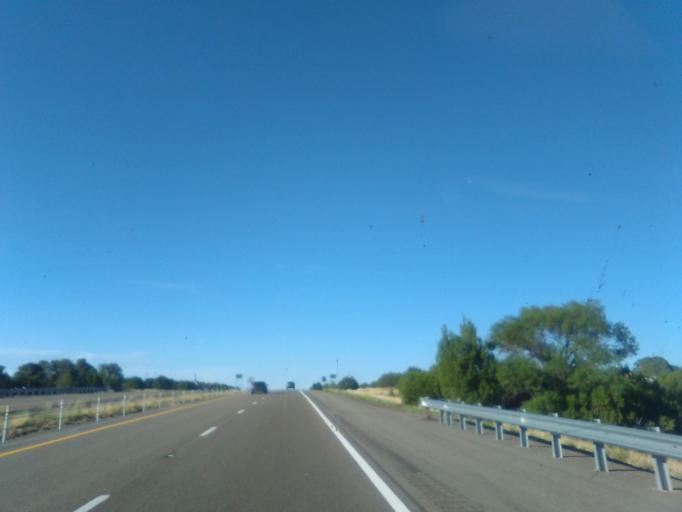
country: US
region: New Mexico
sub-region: San Miguel County
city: Las Vegas
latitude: 35.4941
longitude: -105.2679
